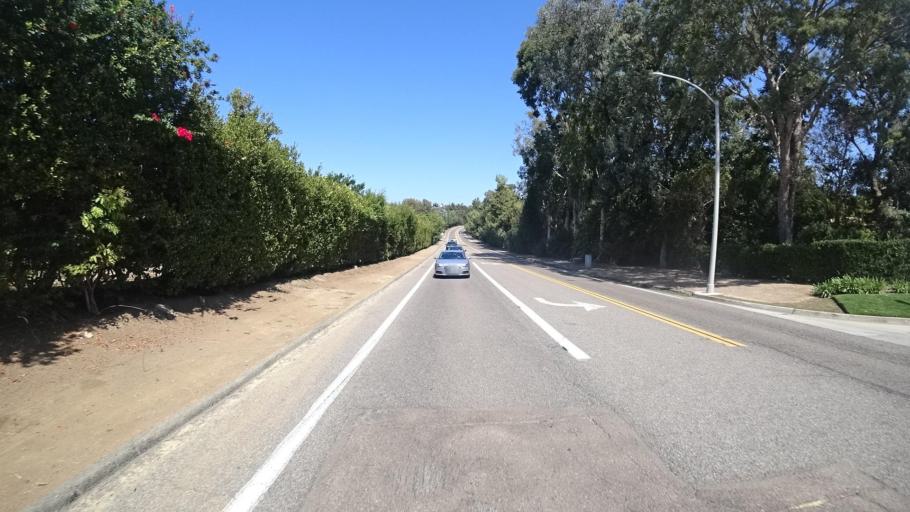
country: US
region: California
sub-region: San Diego County
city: Fairbanks Ranch
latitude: 33.0004
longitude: -117.1789
